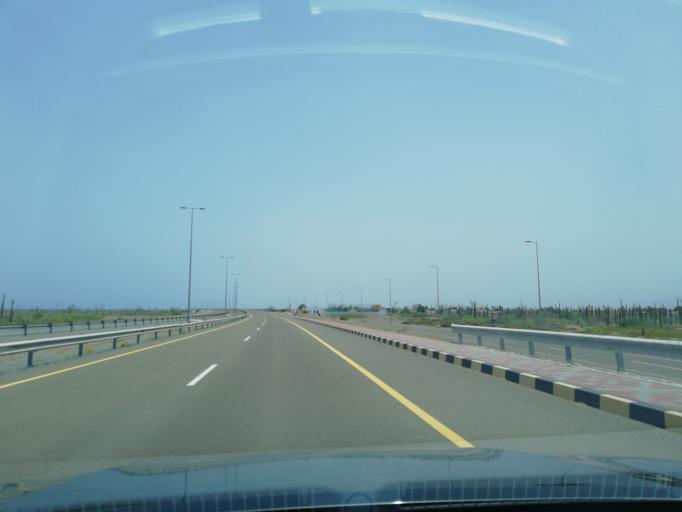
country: OM
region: Al Batinah
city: Shinas
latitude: 24.8750
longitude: 56.4058
